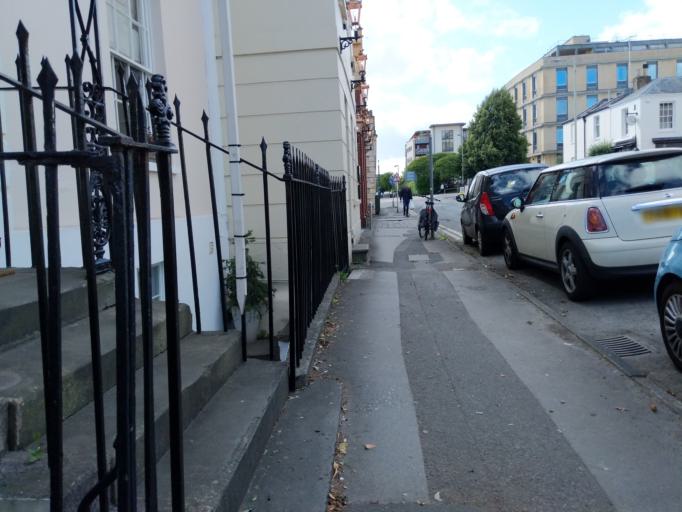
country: GB
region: England
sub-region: Gloucestershire
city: Cheltenham
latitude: 51.9003
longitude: -2.0802
